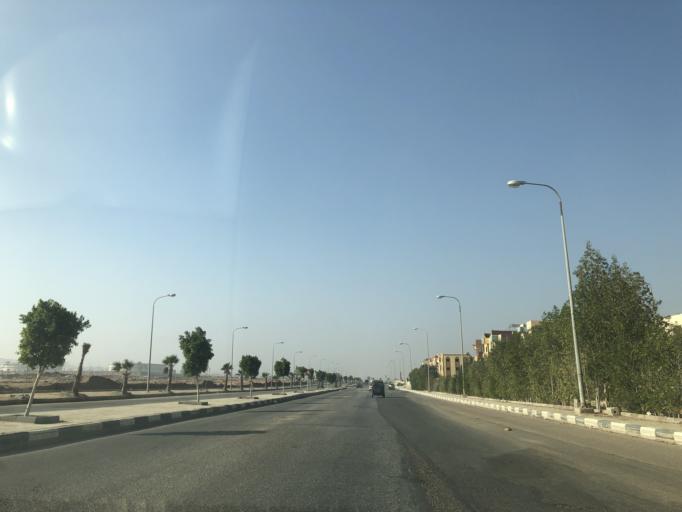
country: EG
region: Al Jizah
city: Madinat Sittah Uktubar
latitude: 29.9302
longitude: 31.0474
